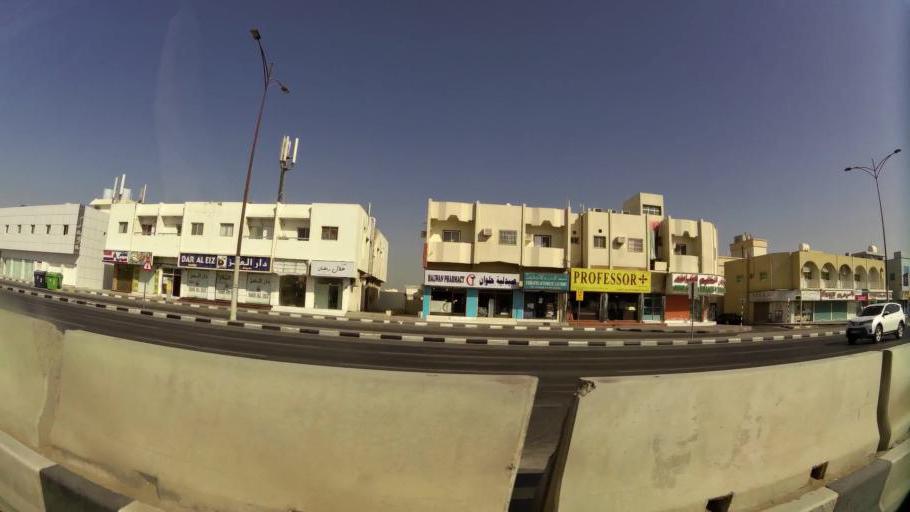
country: AE
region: Ash Shariqah
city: Sharjah
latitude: 25.3419
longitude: 55.4301
